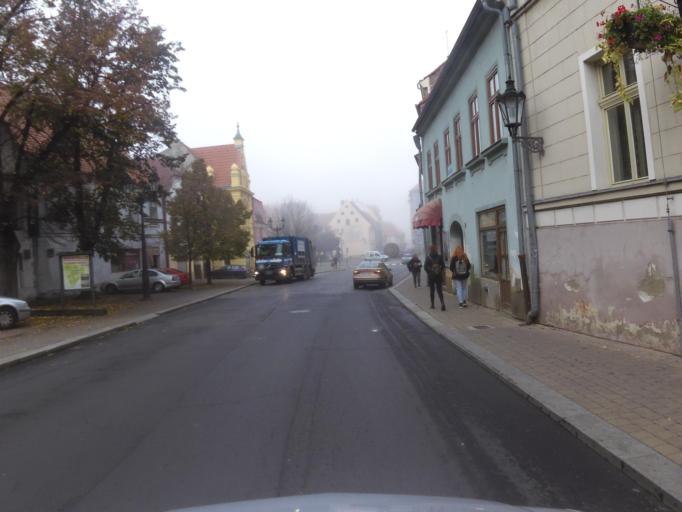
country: CZ
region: Ustecky
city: Zatec
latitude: 50.3261
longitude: 13.5464
